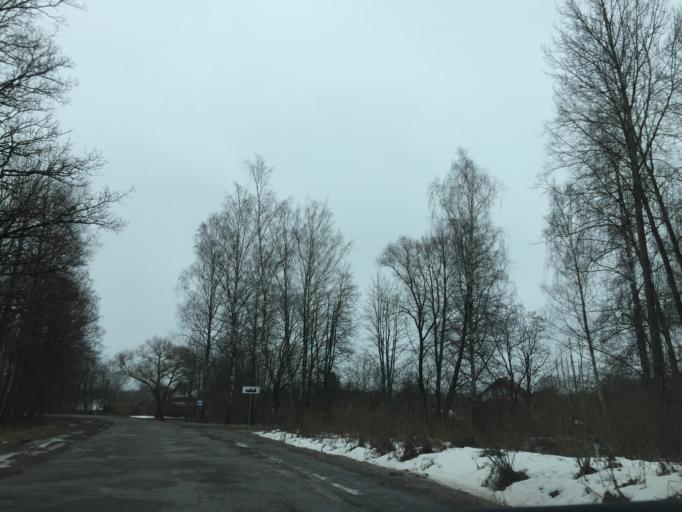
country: LV
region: Ozolnieku
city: Ozolnieki
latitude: 56.6319
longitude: 23.7751
